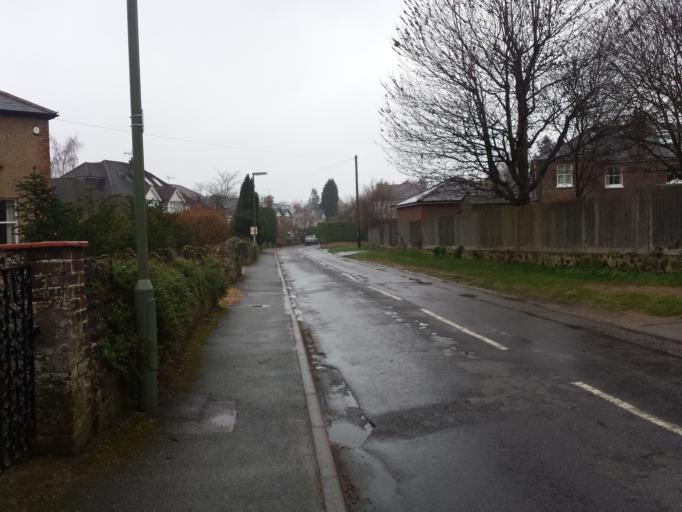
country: GB
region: England
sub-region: Surrey
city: Godalming
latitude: 51.1778
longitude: -0.6096
